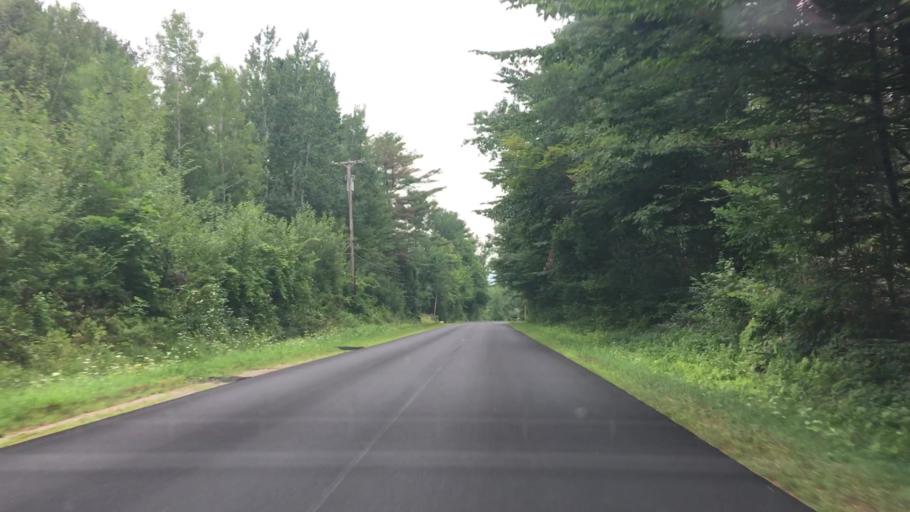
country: US
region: New York
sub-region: Clinton County
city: Peru
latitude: 44.5814
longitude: -73.5703
